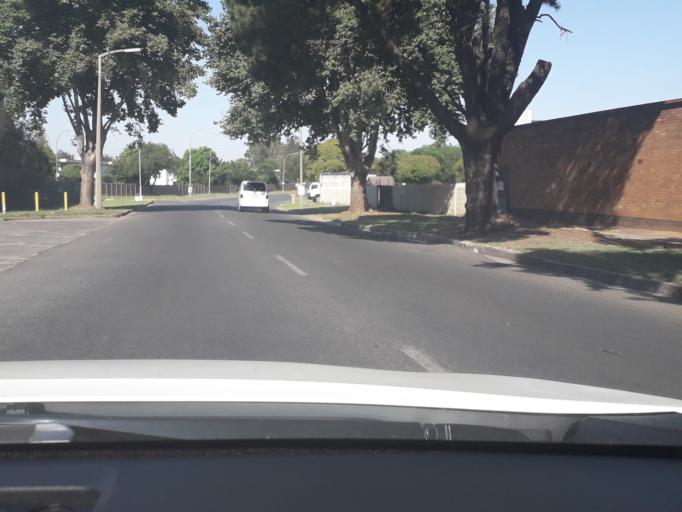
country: ZA
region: Gauteng
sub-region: Ekurhuleni Metropolitan Municipality
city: Benoni
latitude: -26.1969
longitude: 28.3073
